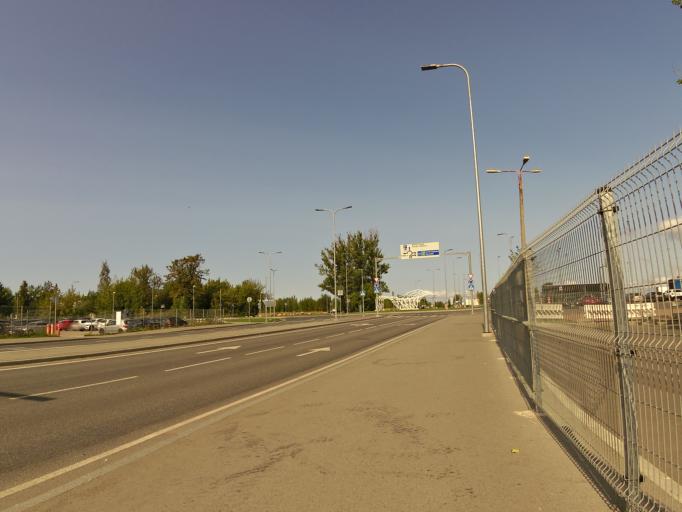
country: EE
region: Harju
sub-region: Tallinna linn
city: Tallinn
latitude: 59.4445
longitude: 24.7588
